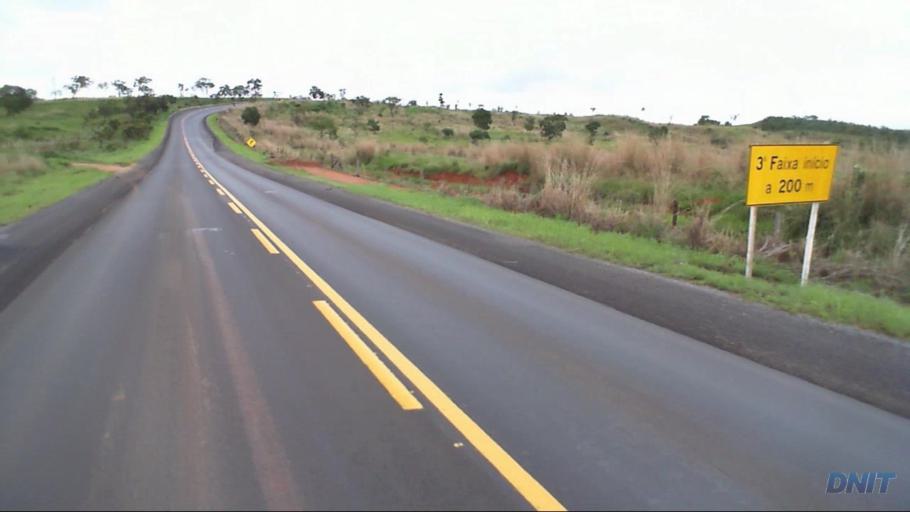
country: BR
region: Goias
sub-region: Padre Bernardo
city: Padre Bernardo
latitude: -15.2098
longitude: -48.4725
